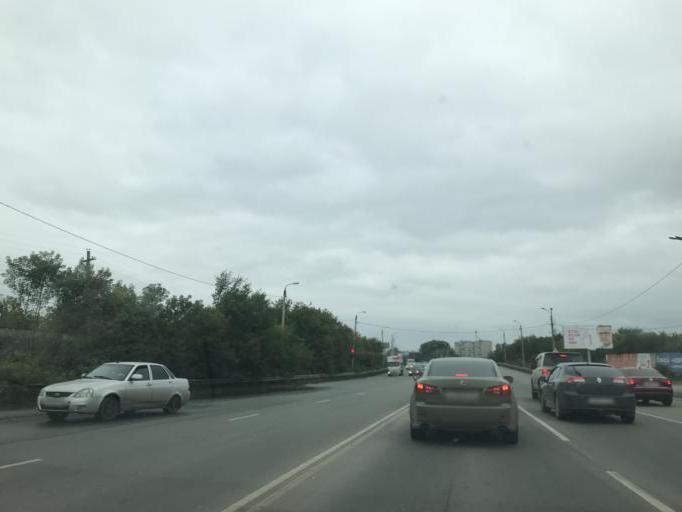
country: RU
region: Chelyabinsk
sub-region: Gorod Chelyabinsk
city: Chelyabinsk
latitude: 55.1655
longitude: 61.4283
